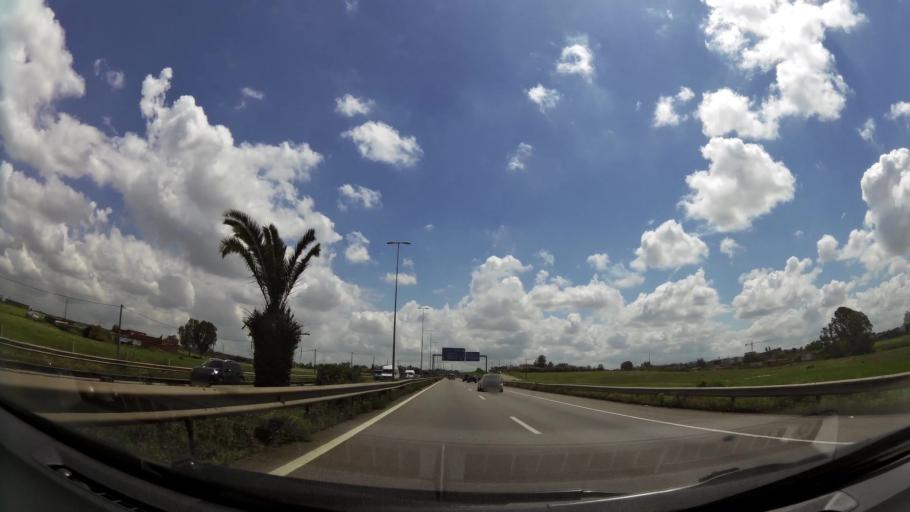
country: MA
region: Grand Casablanca
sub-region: Nouaceur
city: Bouskoura
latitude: 33.4458
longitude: -7.6322
